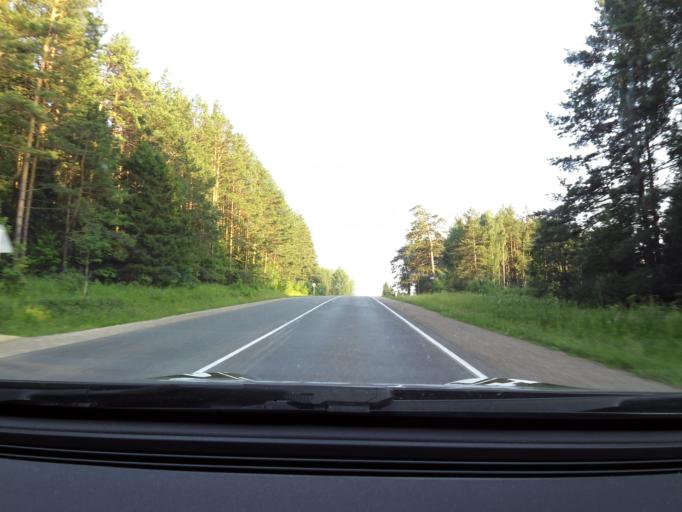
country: RU
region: Sverdlovsk
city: Nizhniye Sergi
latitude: 56.5666
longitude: 59.2152
